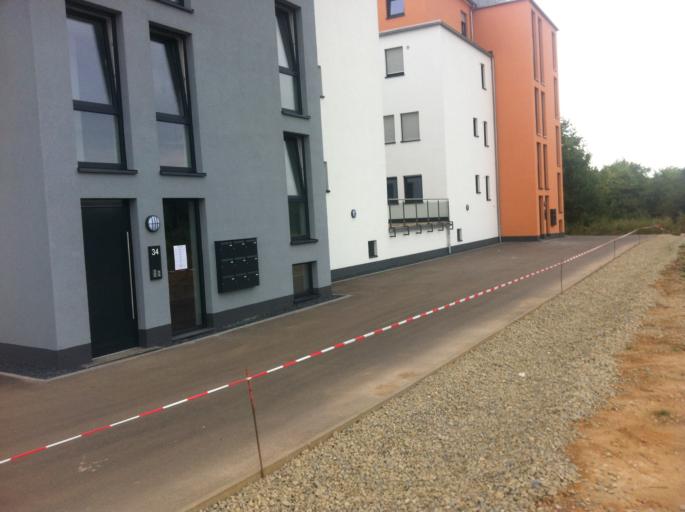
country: DE
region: Saarland
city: Perl
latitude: 49.4792
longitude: 6.3825
